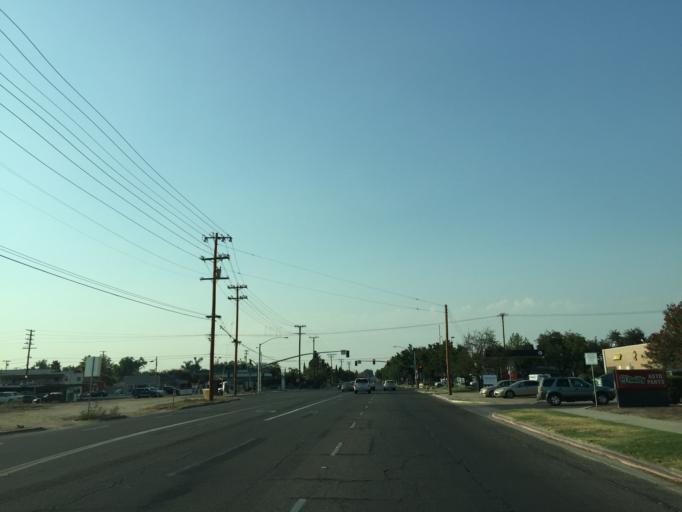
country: US
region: California
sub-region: Tulare County
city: Visalia
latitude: 36.3407
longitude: -119.2788
